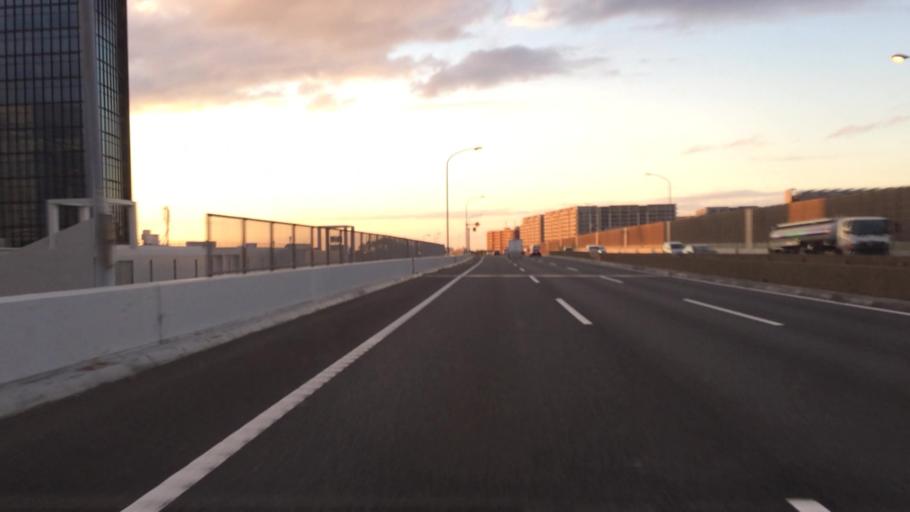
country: JP
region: Chiba
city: Funabashi
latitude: 35.6552
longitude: 140.0417
